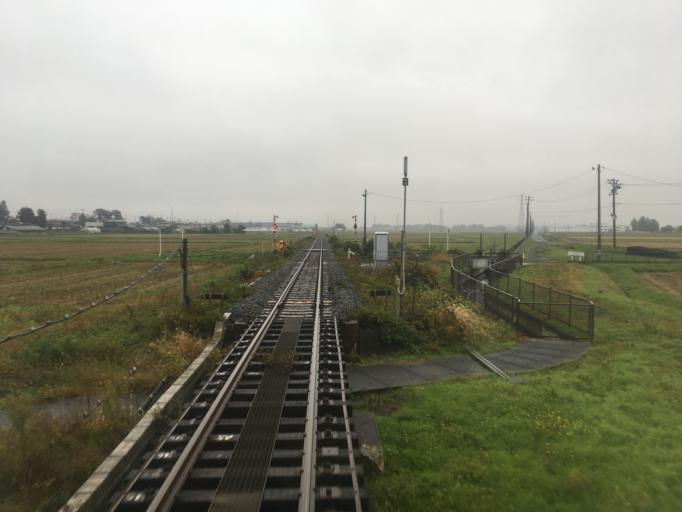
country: JP
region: Miyagi
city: Kogota
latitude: 38.5625
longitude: 141.0115
